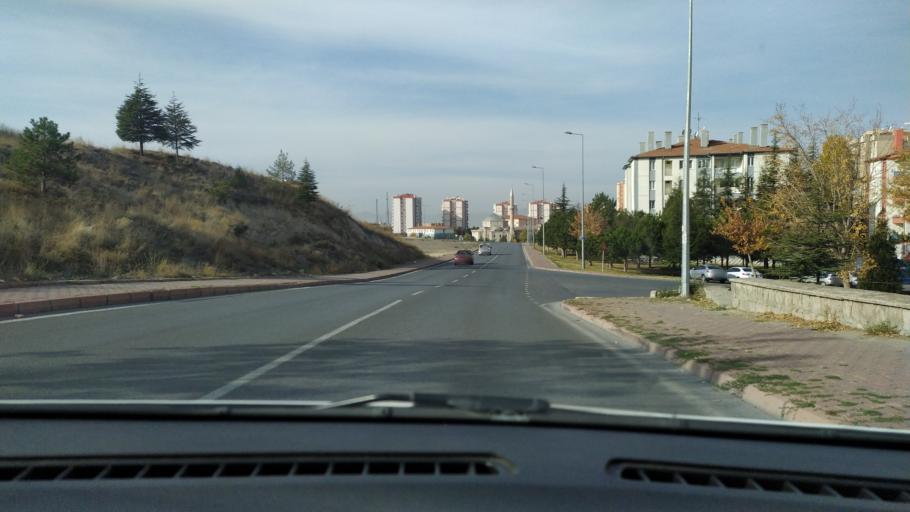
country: TR
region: Kayseri
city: Melikgazi
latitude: 38.7355
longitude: 35.3864
